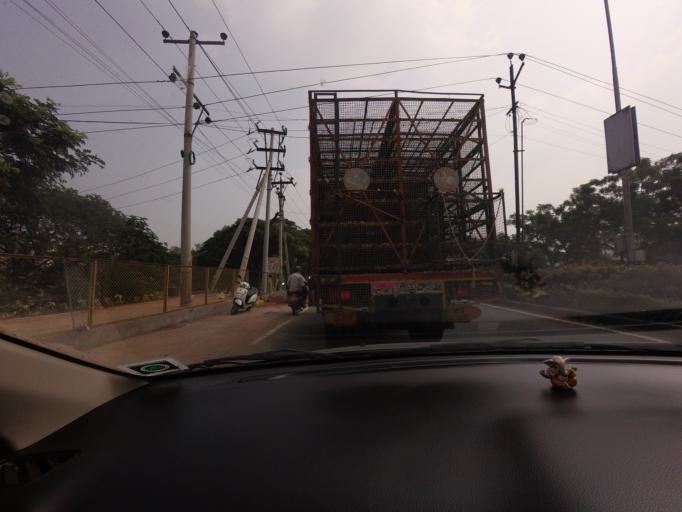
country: IN
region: Andhra Pradesh
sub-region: Krishna
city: Vijayawada
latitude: 16.4976
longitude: 80.6411
